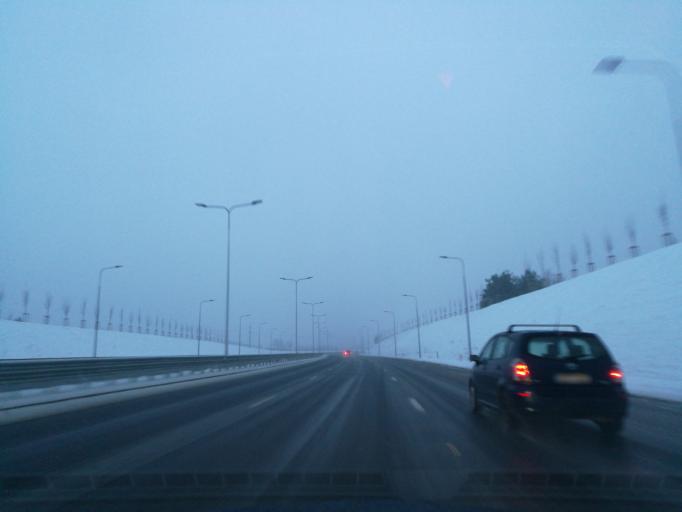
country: LT
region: Vilnius County
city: Justiniskes
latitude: 54.7088
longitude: 25.2096
